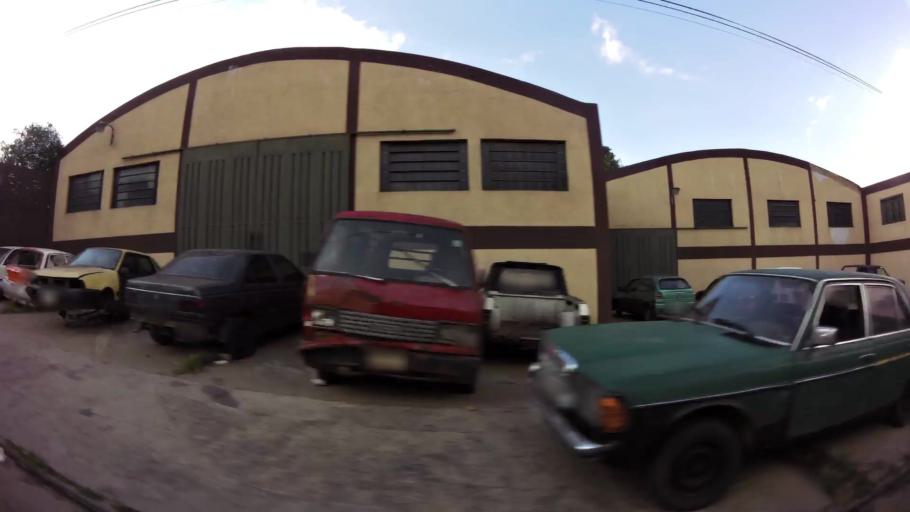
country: PY
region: Central
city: Villa Elisa
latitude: -25.3566
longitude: -57.5639
